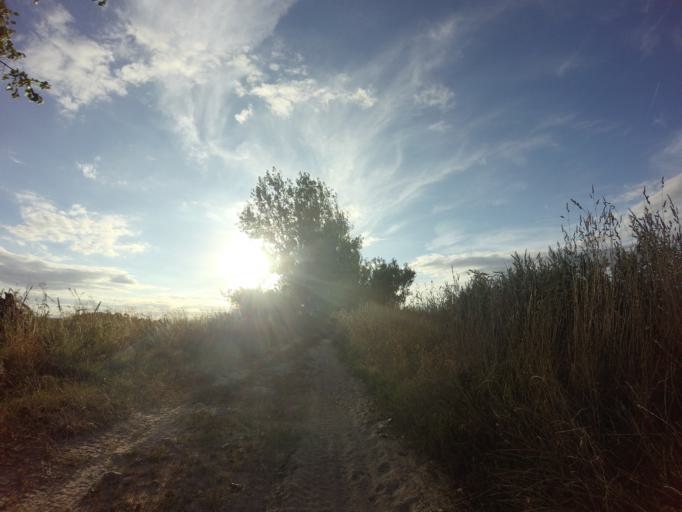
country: PL
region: West Pomeranian Voivodeship
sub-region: Powiat choszczenski
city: Choszczno
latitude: 53.1145
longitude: 15.4320
